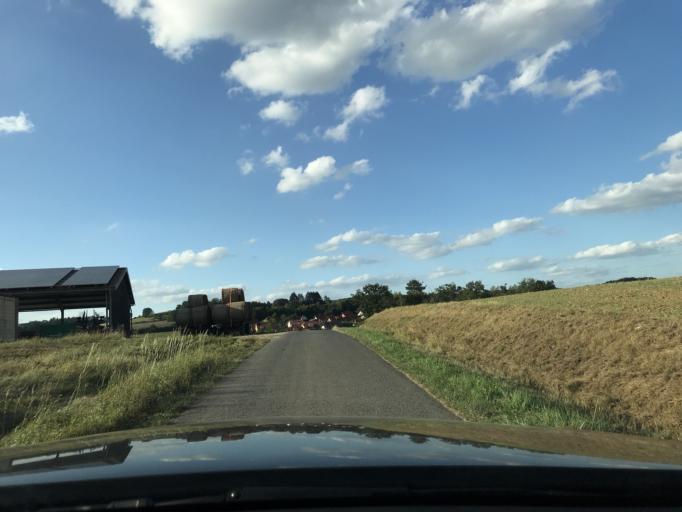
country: DE
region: Bavaria
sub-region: Regierungsbezirk Unterfranken
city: Breitbrunn
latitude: 50.0278
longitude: 10.6843
